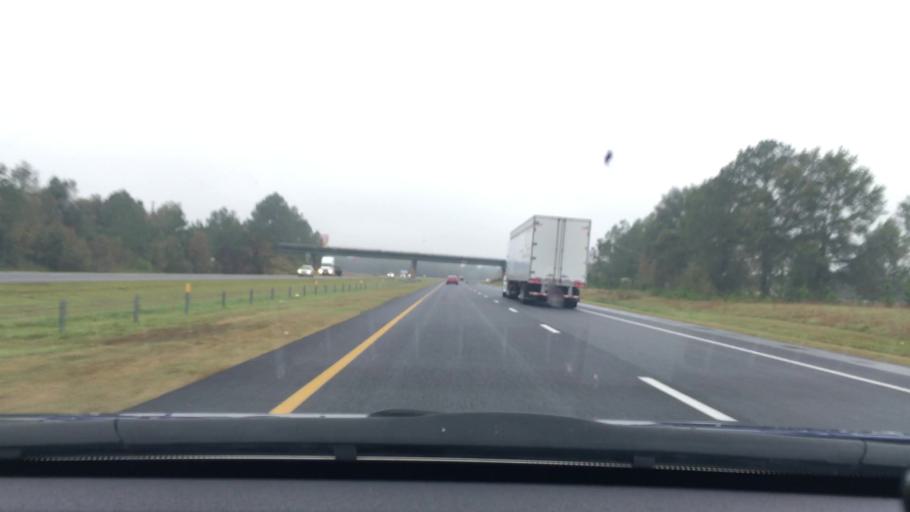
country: US
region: South Carolina
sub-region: Florence County
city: Timmonsville
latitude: 34.2009
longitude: -80.0672
